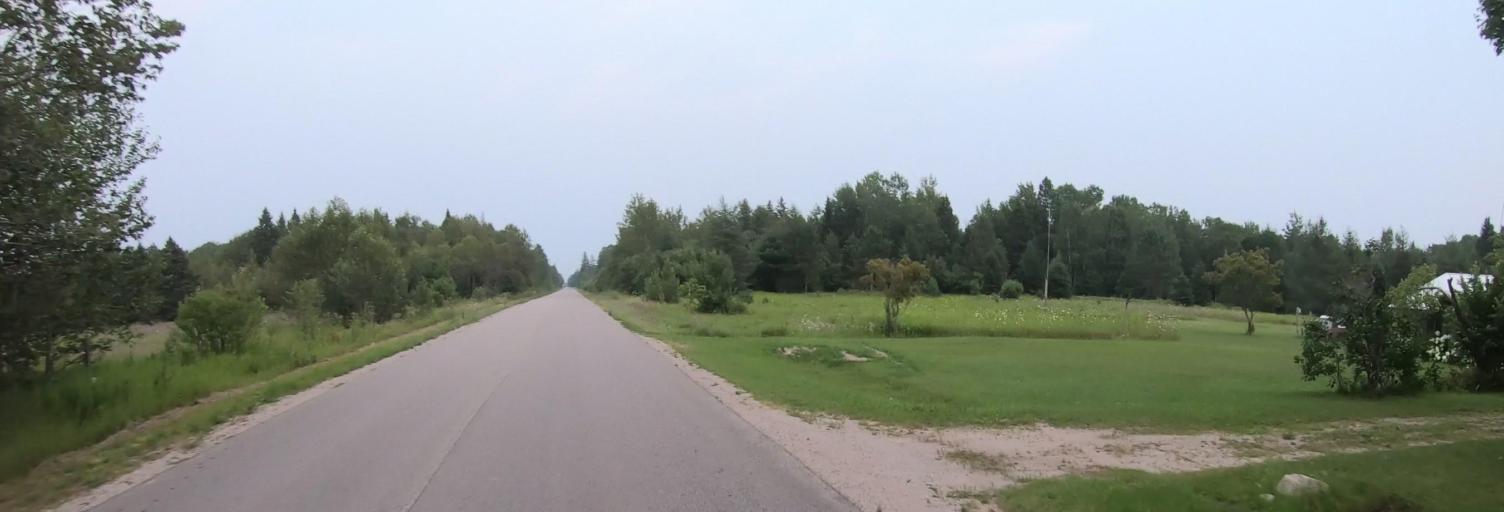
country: US
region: Michigan
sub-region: Mackinac County
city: Saint Ignace
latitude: 45.6945
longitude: -84.8014
